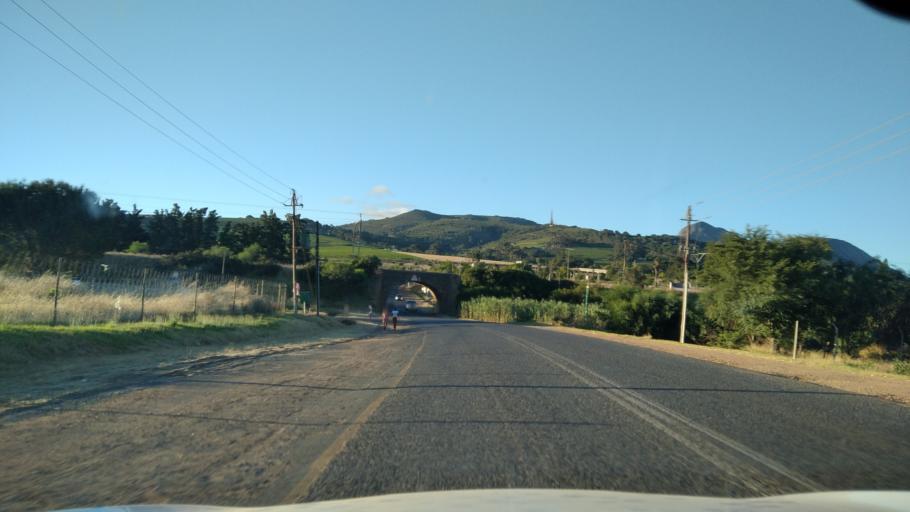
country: ZA
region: Western Cape
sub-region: Cape Winelands District Municipality
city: Paarl
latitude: -33.7860
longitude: 18.9532
